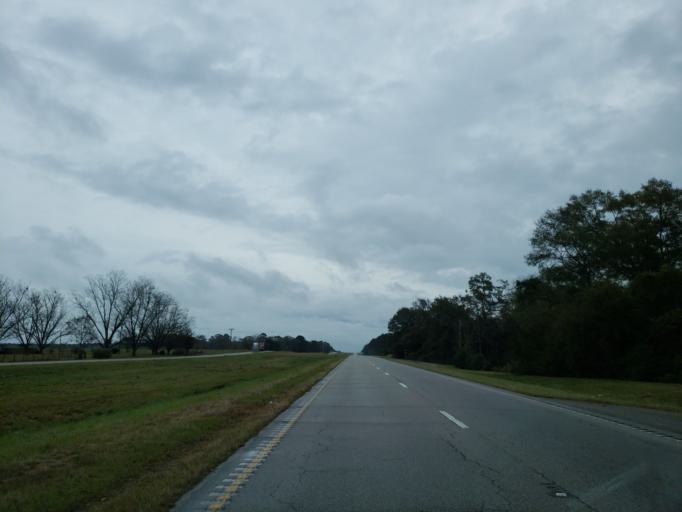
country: US
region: Mississippi
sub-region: Jones County
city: Sharon
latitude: 31.6967
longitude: -88.8891
